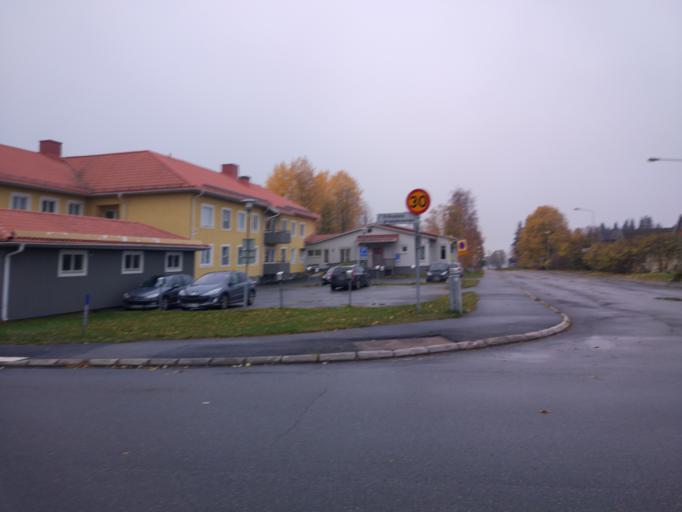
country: SE
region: Vaesterbotten
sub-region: Umea Kommun
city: Holmsund
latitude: 63.6985
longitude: 20.3678
